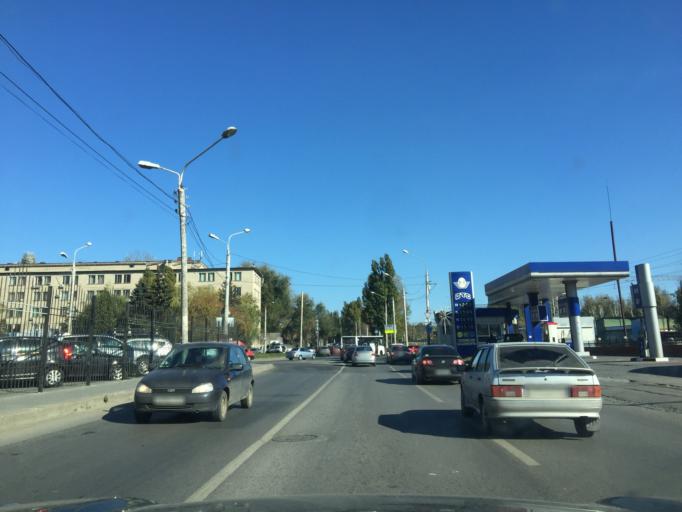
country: RU
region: Rostov
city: Imeni Chkalova
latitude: 47.2480
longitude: 39.7568
